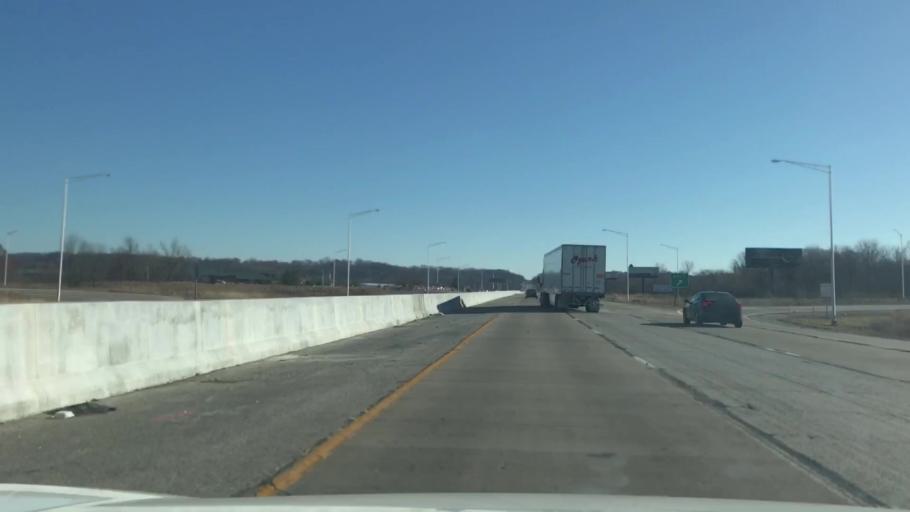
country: US
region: Illinois
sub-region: Saint Clair County
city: Alorton
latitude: 38.5821
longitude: -90.1075
